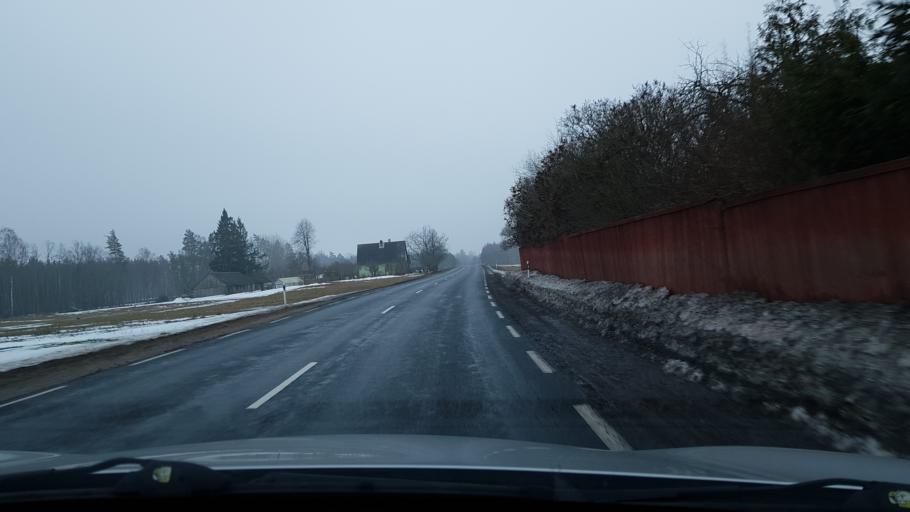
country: EE
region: Valgamaa
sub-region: Torva linn
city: Torva
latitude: 58.1285
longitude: 25.9923
